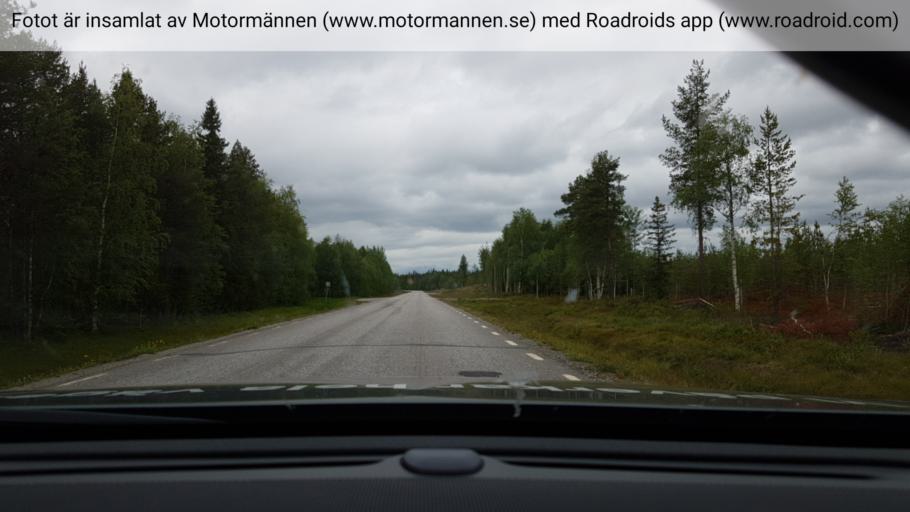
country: SE
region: Vaesterbotten
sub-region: Sorsele Kommun
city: Sorsele
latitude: 65.3075
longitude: 17.7053
